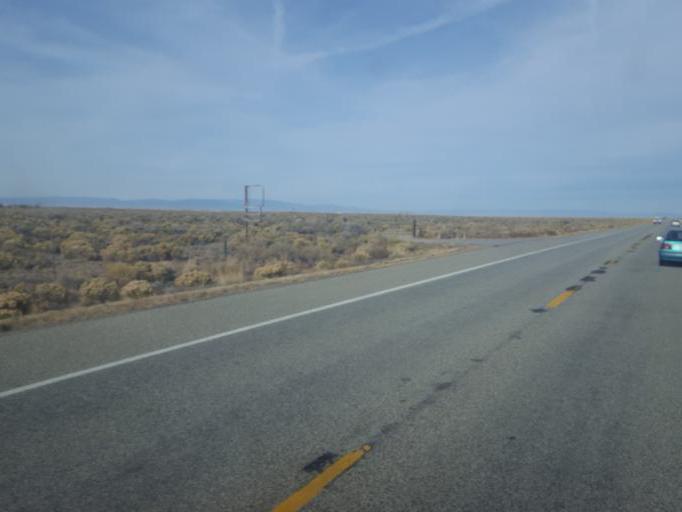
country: US
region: Colorado
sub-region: Costilla County
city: San Luis
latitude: 37.4460
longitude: -105.5356
